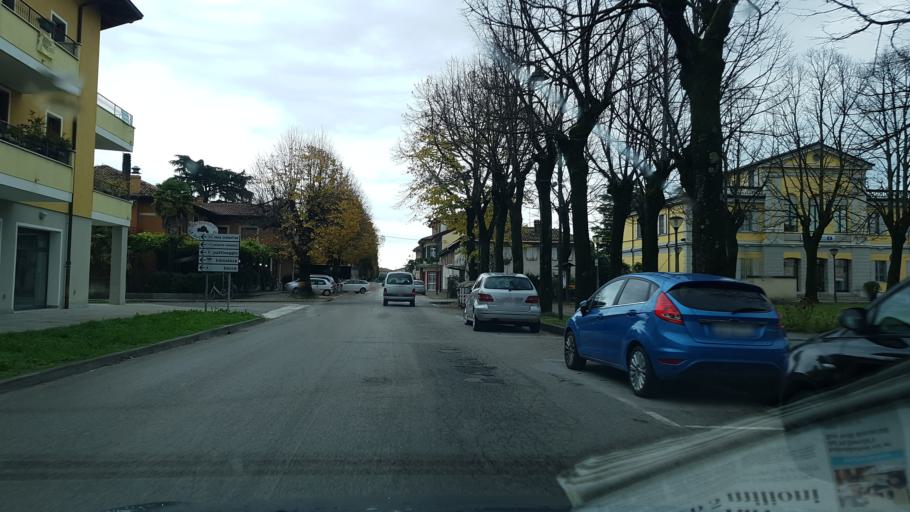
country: IT
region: Friuli Venezia Giulia
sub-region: Provincia di Udine
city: Fiumicello
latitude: 45.7913
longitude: 13.4093
